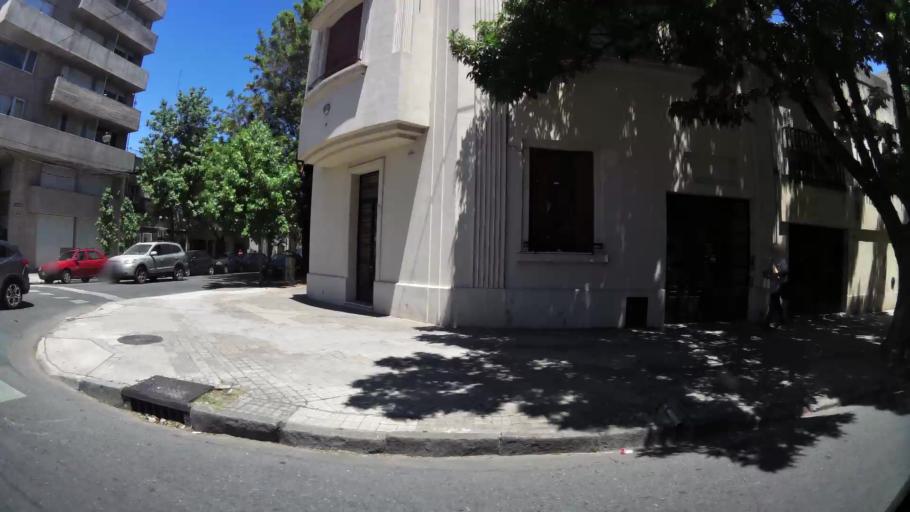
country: AR
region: Santa Fe
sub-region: Departamento de Rosario
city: Rosario
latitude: -32.9468
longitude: -60.6586
